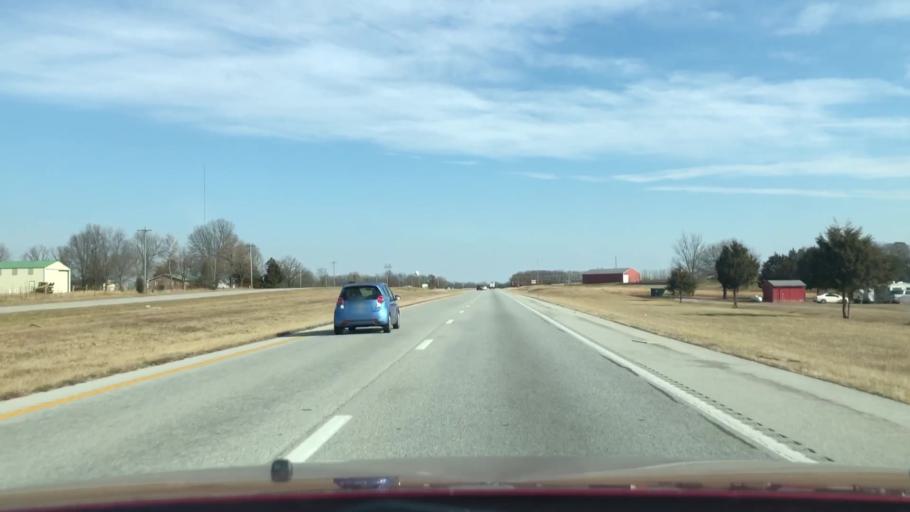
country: US
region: Missouri
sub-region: Webster County
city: Rogersville
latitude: 37.1429
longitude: -92.9576
